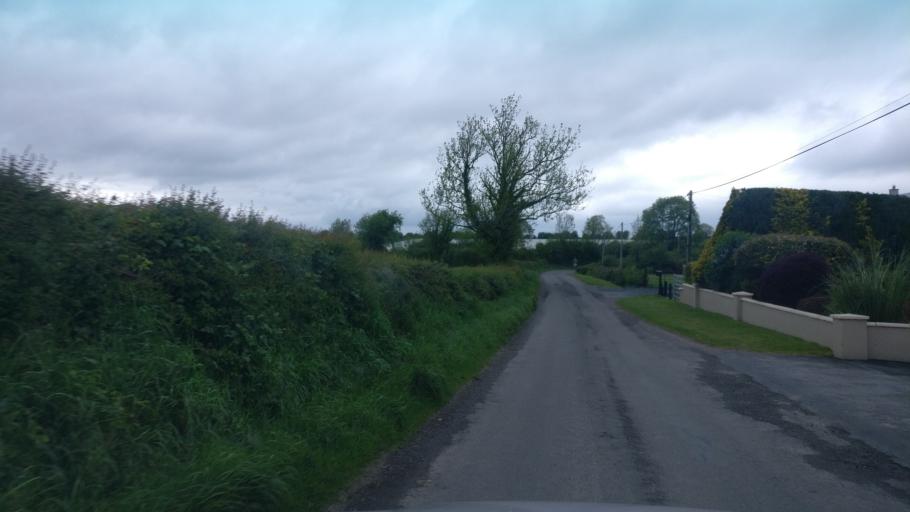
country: IE
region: Connaught
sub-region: County Galway
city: Portumna
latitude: 53.1328
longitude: -8.2916
